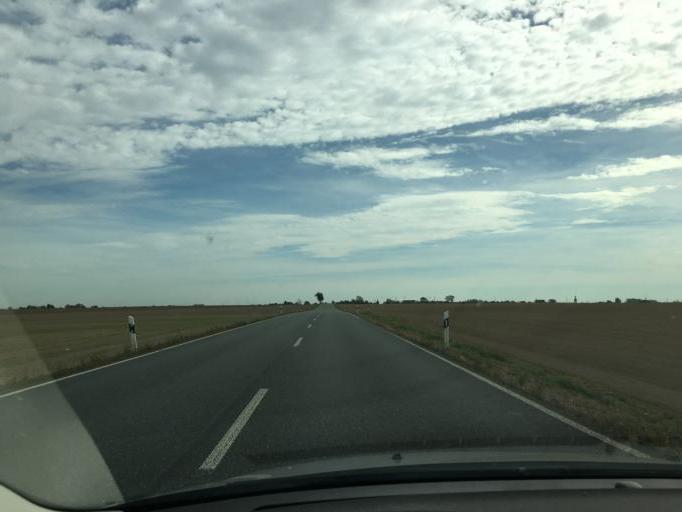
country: DE
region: Saxony
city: Riesa
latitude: 51.2581
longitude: 13.2725
